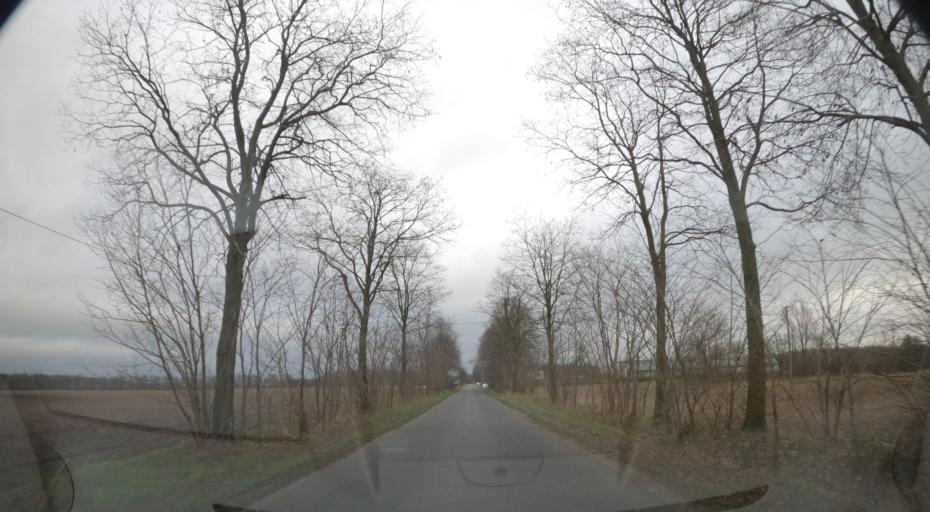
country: PL
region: Greater Poland Voivodeship
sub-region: Powiat pilski
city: Lobzenica
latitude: 53.2605
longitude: 17.1725
